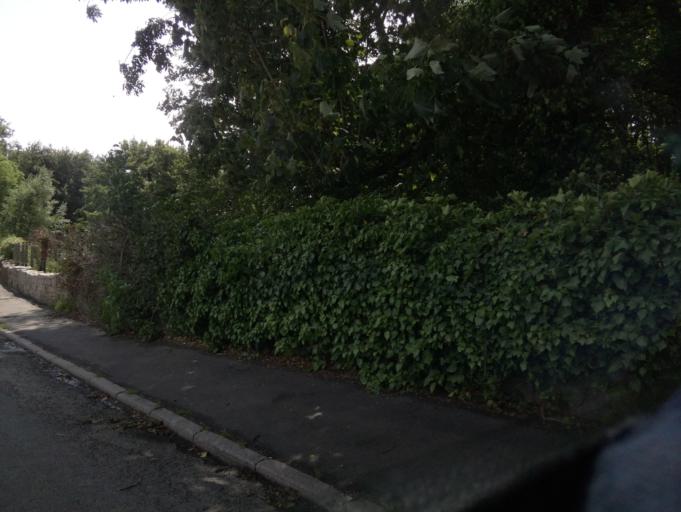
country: GB
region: Wales
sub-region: Vale of Glamorgan
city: Wick
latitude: 51.4093
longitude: -3.5319
